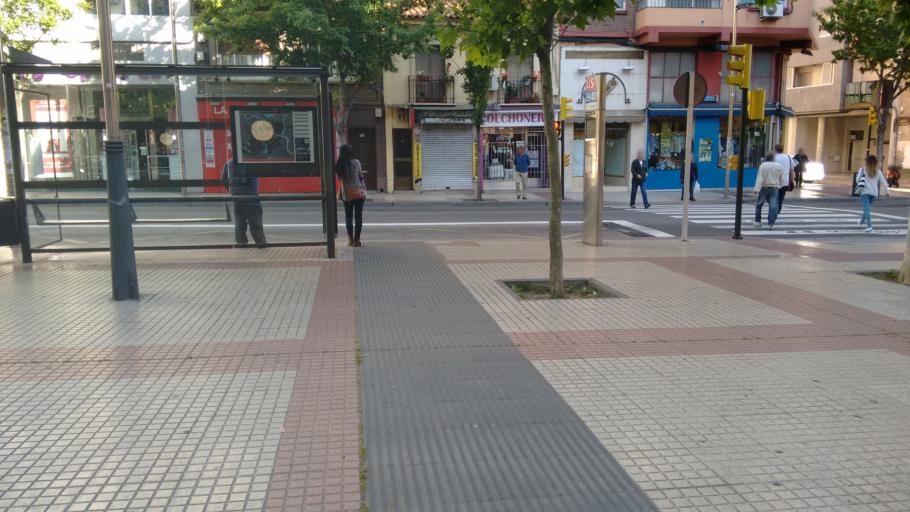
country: ES
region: Aragon
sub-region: Provincia de Zaragoza
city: Zaragoza
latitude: 41.6364
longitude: -0.8780
